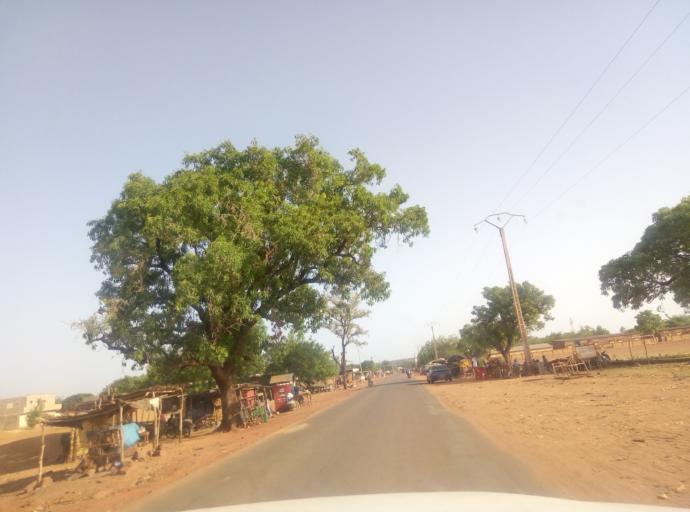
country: ML
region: Bamako
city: Bamako
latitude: 12.5925
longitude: -7.7666
